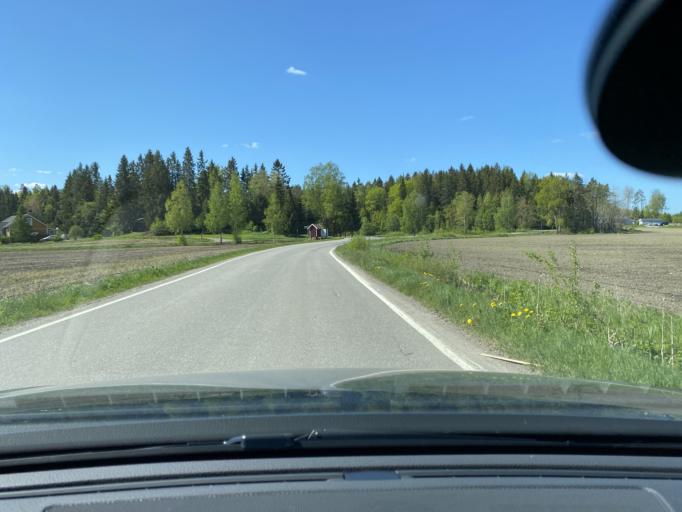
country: FI
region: Varsinais-Suomi
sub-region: Turku
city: Piikkioe
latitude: 60.4597
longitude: 22.5472
